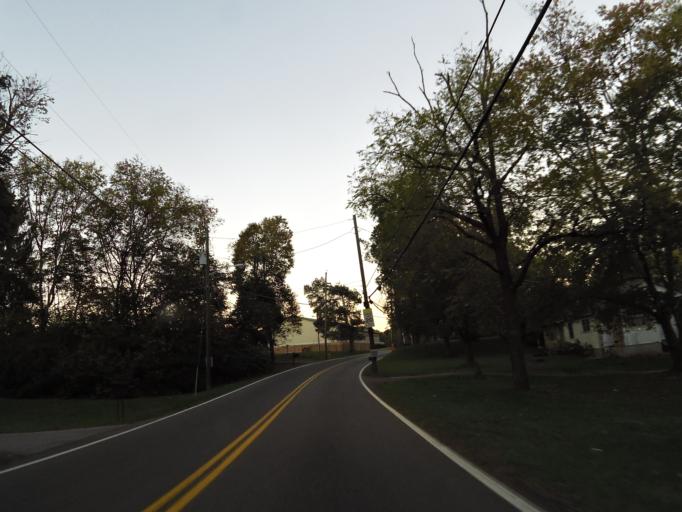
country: US
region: Tennessee
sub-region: Knox County
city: Knoxville
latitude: 36.0284
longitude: -83.9485
